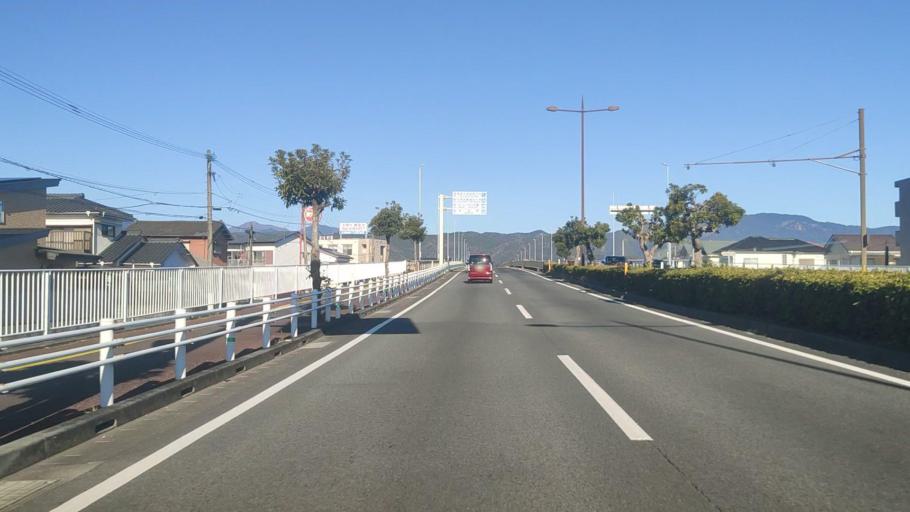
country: JP
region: Miyazaki
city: Nobeoka
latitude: 32.5805
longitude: 131.6817
